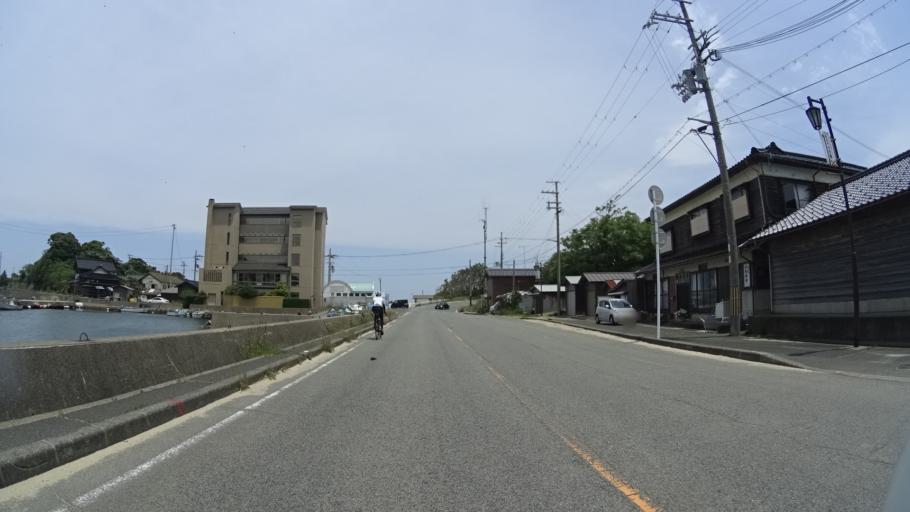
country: JP
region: Hyogo
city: Toyooka
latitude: 35.6445
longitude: 134.9025
